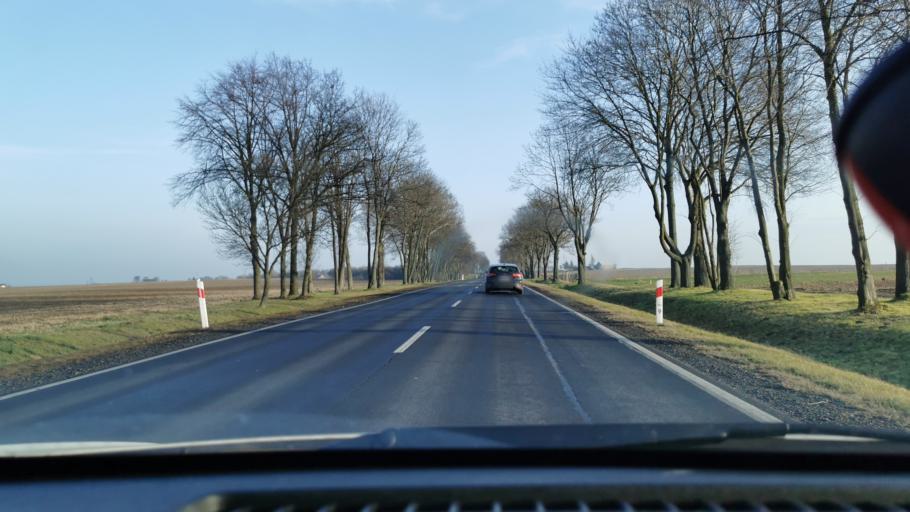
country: PL
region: Lodz Voivodeship
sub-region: Powiat sieradzki
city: Wroblew
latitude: 51.6196
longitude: 18.5885
